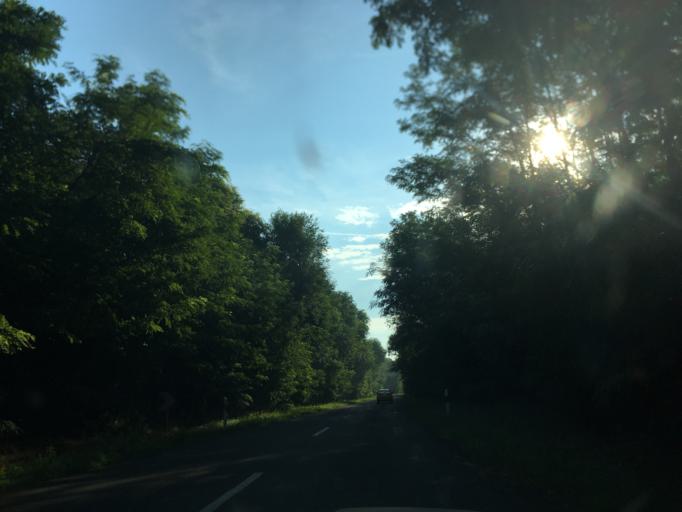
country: HU
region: Hajdu-Bihar
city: Hajdusamson
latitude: 47.5472
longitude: 21.7204
